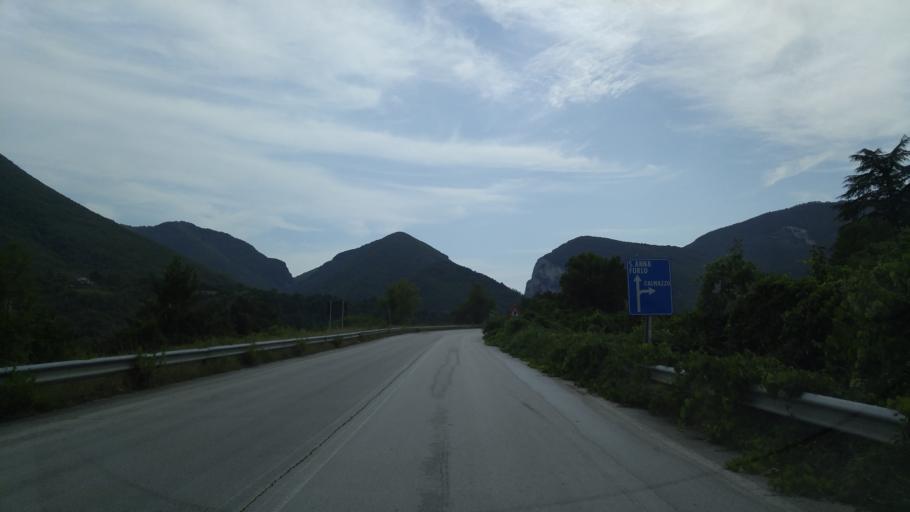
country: IT
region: The Marches
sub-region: Provincia di Pesaro e Urbino
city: Fossombrone
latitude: 43.6658
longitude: 12.7548
